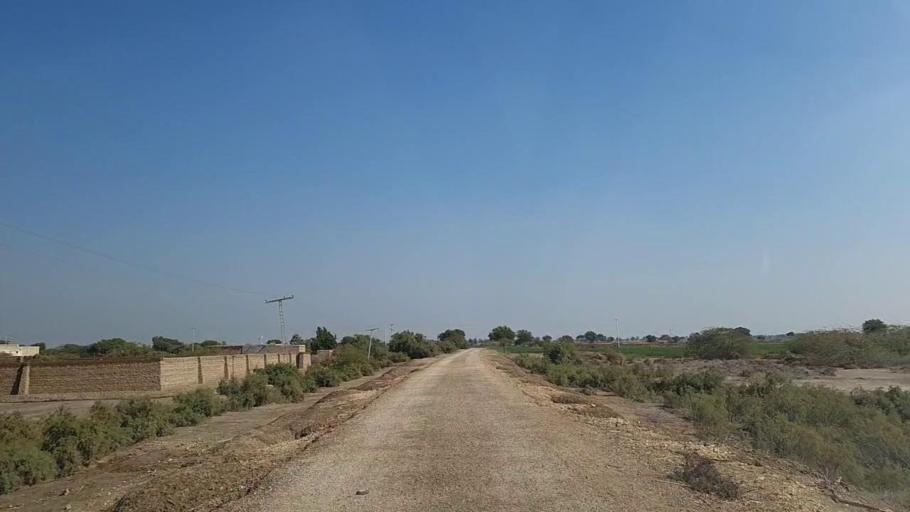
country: PK
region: Sindh
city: Daur
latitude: 26.3596
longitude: 68.3357
